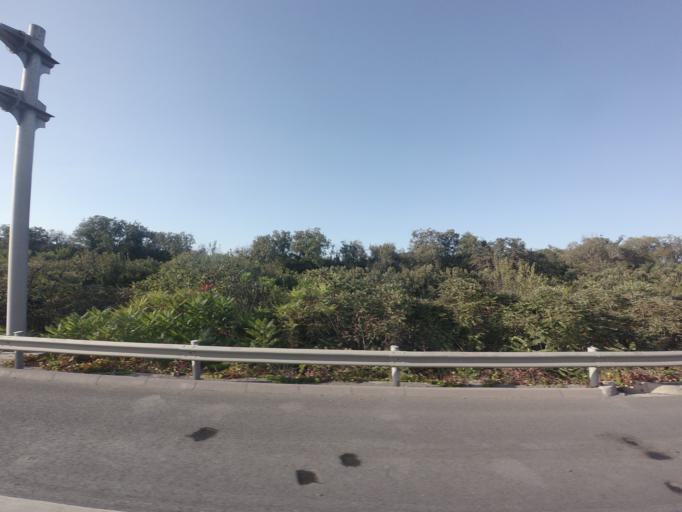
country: CN
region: Beijing
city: Jugezhuang
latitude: 40.3914
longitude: 116.9029
